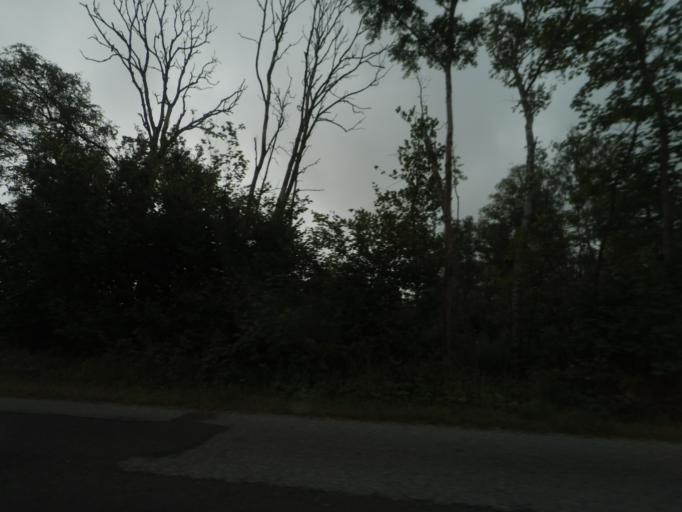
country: DK
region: South Denmark
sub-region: Nordfyns Kommune
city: Otterup
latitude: 55.5671
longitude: 10.3906
